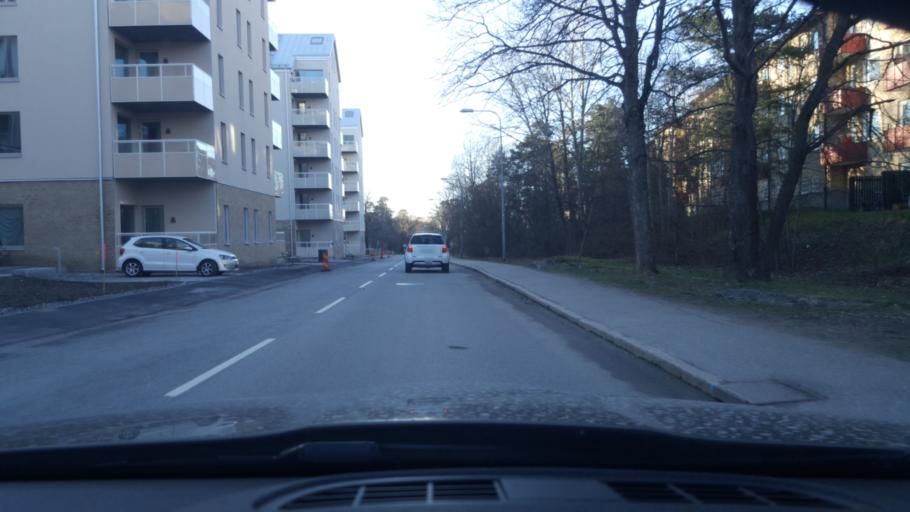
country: SE
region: Stockholm
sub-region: Stockholms Kommun
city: Arsta
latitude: 59.2663
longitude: 18.0563
